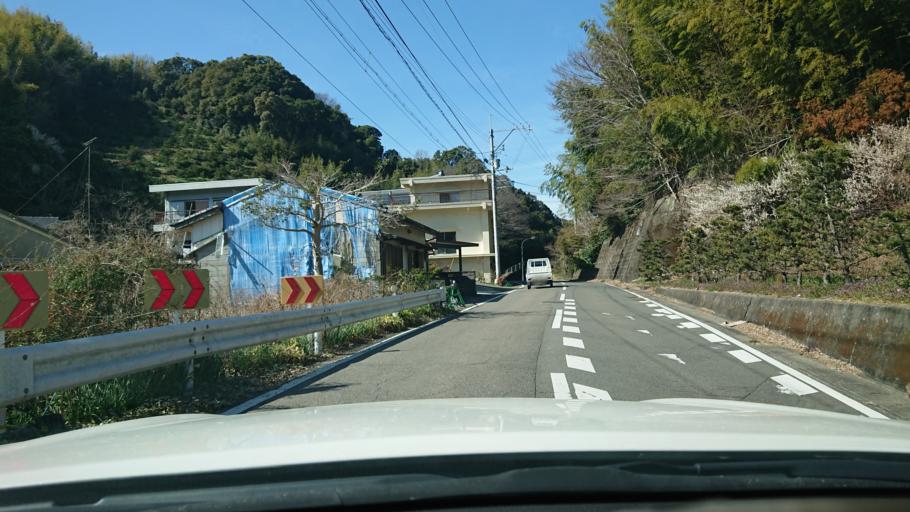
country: JP
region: Tokushima
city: Komatsushimacho
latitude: 33.9705
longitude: 134.5935
